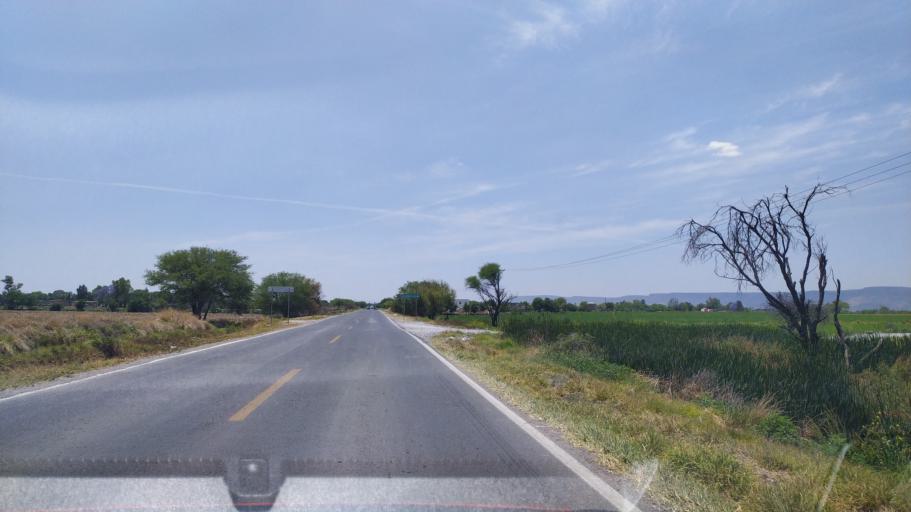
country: MX
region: Guanajuato
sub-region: San Francisco del Rincon
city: San Roque de Montes
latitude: 21.0201
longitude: -101.7912
